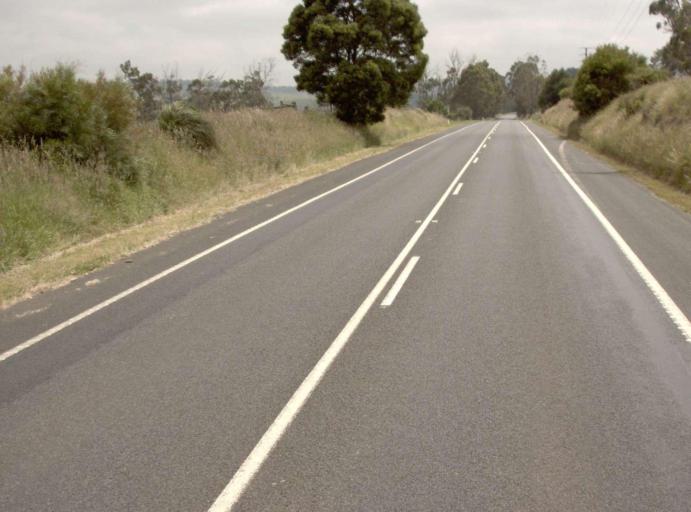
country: AU
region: Victoria
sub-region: Baw Baw
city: Warragul
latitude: -38.4178
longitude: 146.0429
